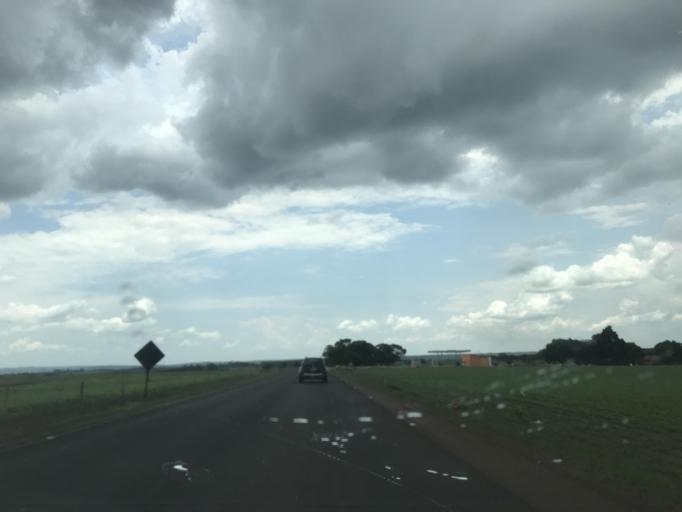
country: BR
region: Goias
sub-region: Vianopolis
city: Vianopolis
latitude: -16.9077
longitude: -48.5527
